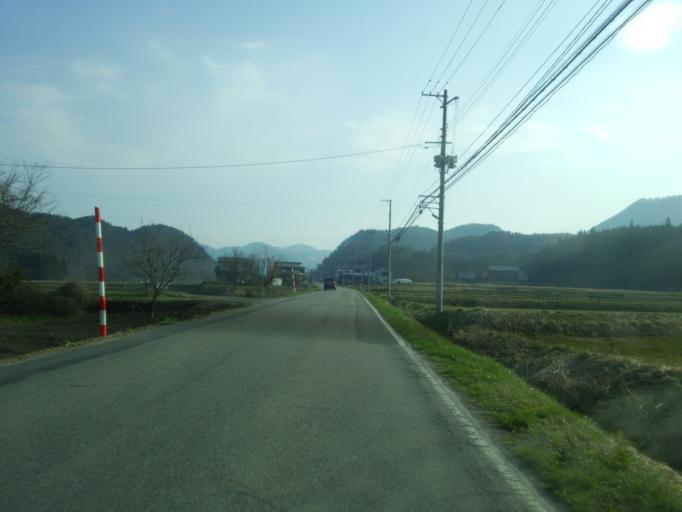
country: JP
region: Fukushima
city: Kitakata
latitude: 37.6831
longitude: 139.9016
